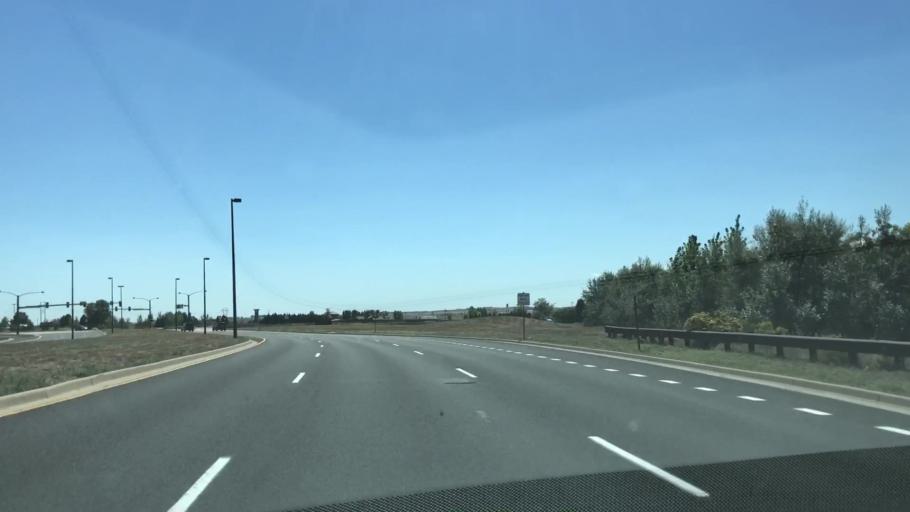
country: US
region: Colorado
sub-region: Larimer County
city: Loveland
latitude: 40.4135
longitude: -104.9870
